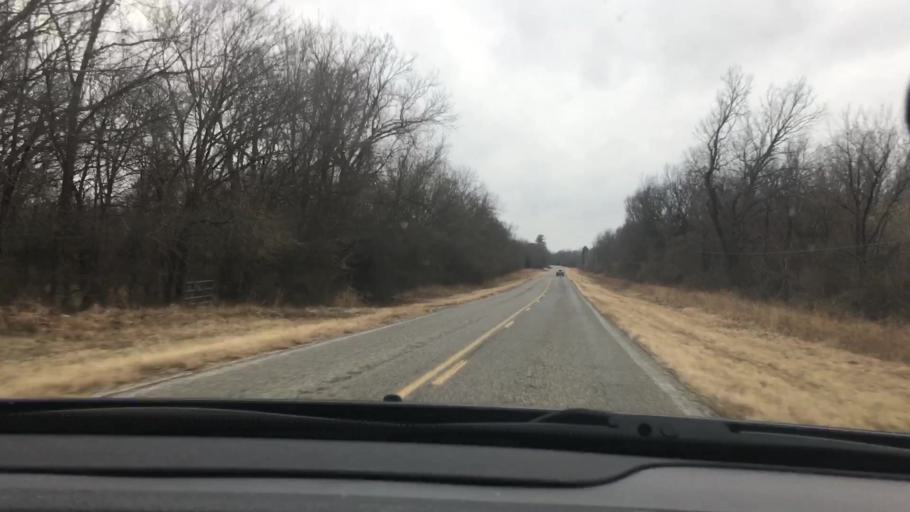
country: US
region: Oklahoma
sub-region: Johnston County
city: Tishomingo
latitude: 34.2172
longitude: -96.6361
